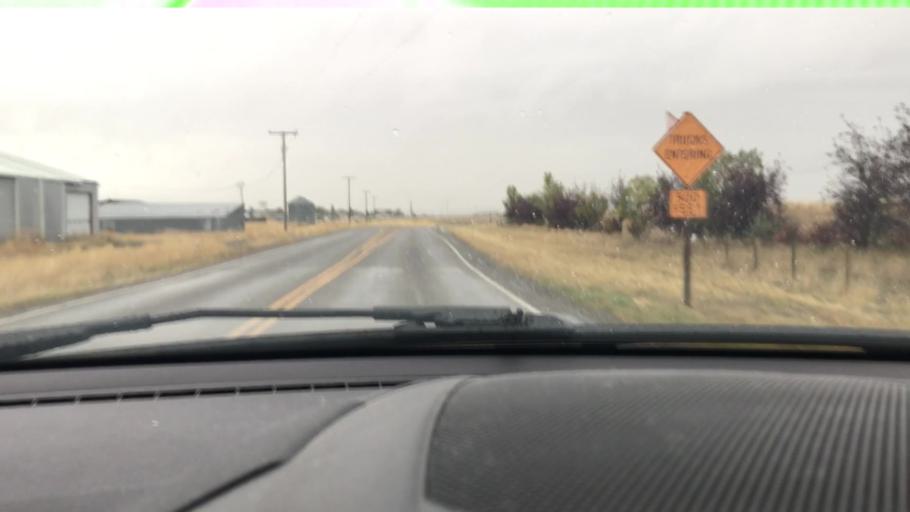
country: US
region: Montana
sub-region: Gallatin County
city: Belgrade
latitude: 45.7544
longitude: -111.1646
